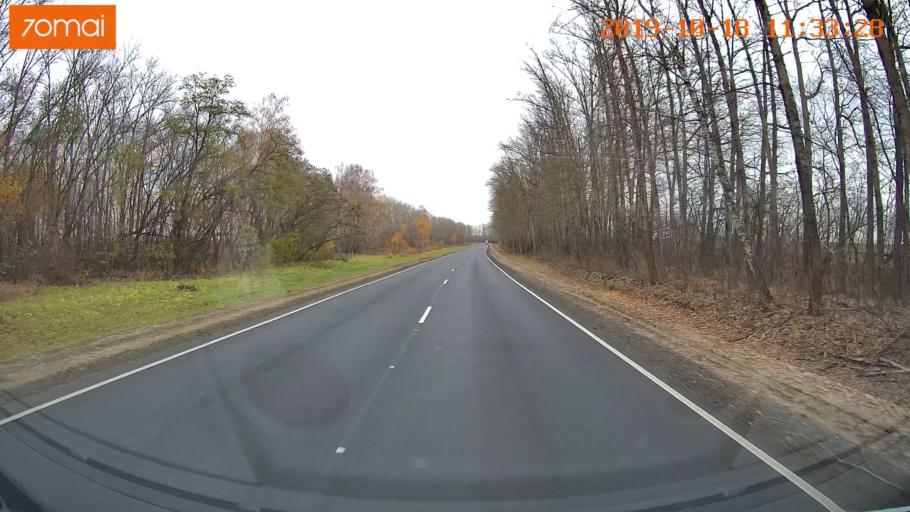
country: RU
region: Rjazan
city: Oktyabr'skiy
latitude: 54.1409
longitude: 38.7412
